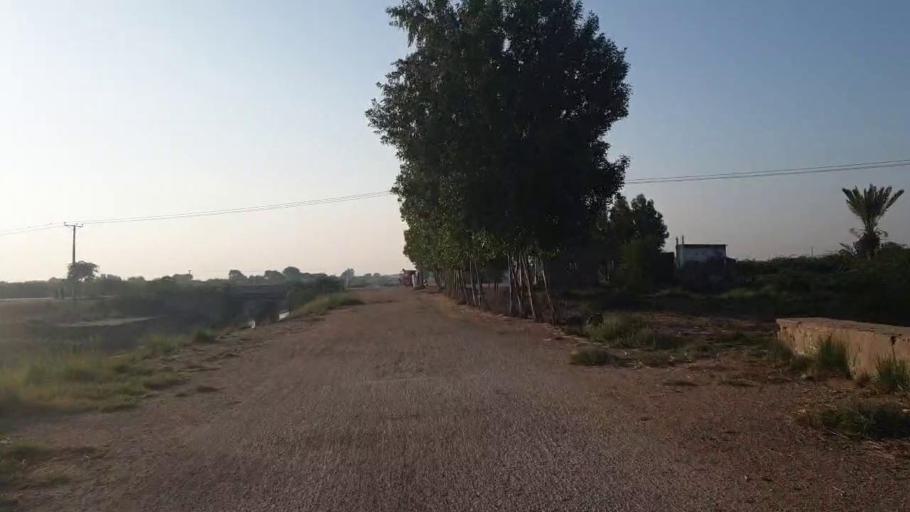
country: PK
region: Sindh
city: Badin
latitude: 24.6500
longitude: 68.7893
